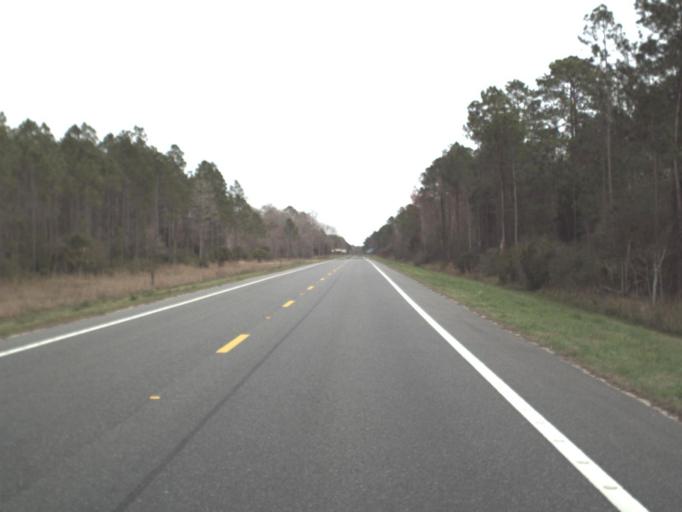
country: US
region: Florida
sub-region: Leon County
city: Woodville
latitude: 30.1901
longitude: -84.0563
